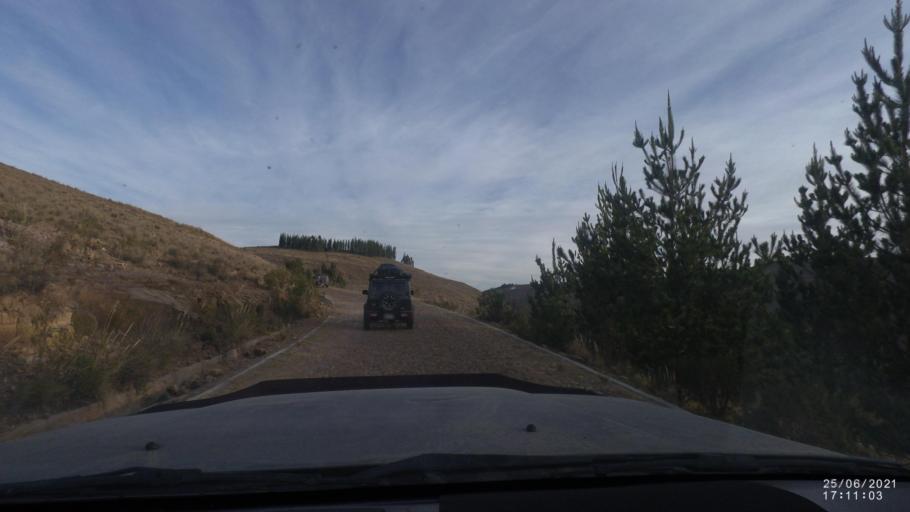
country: BO
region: Cochabamba
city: Arani
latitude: -17.8435
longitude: -65.7046
